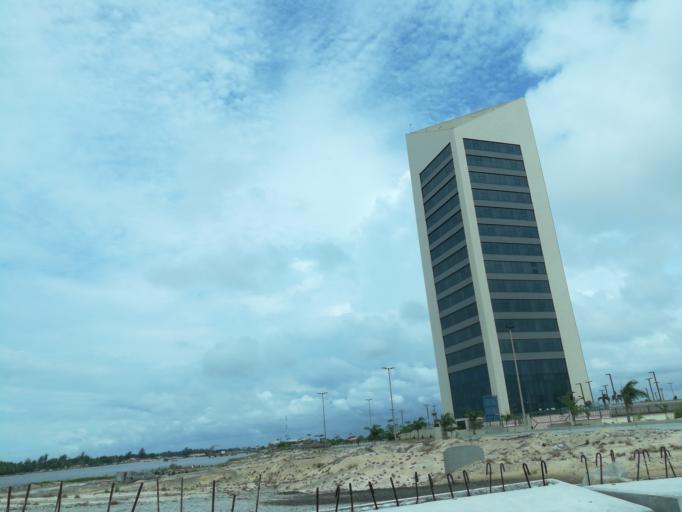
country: NG
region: Lagos
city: Lagos
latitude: 6.4061
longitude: 3.4042
